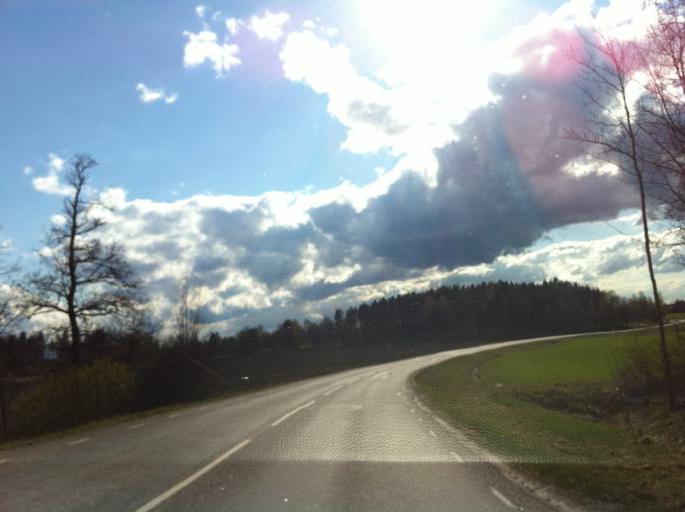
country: SE
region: Soedermanland
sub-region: Eskilstuna Kommun
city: Eskilstuna
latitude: 59.4162
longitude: 16.5180
